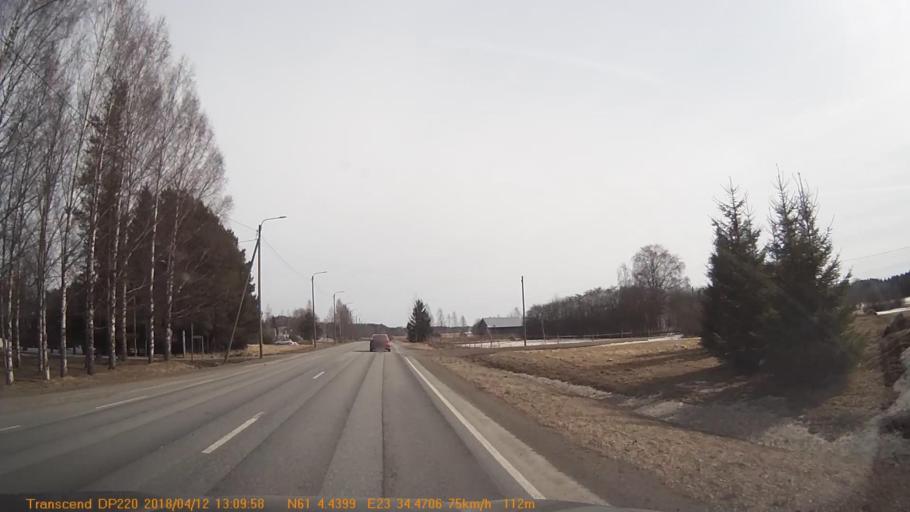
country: FI
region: Pirkanmaa
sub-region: Etelae-Pirkanmaa
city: Urjala
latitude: 61.0737
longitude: 23.5763
